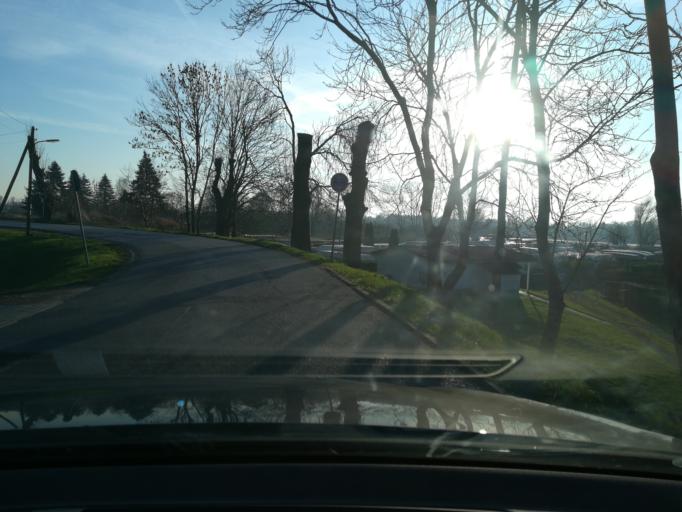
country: DE
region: Lower Saxony
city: Stelle
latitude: 53.4417
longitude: 10.1114
